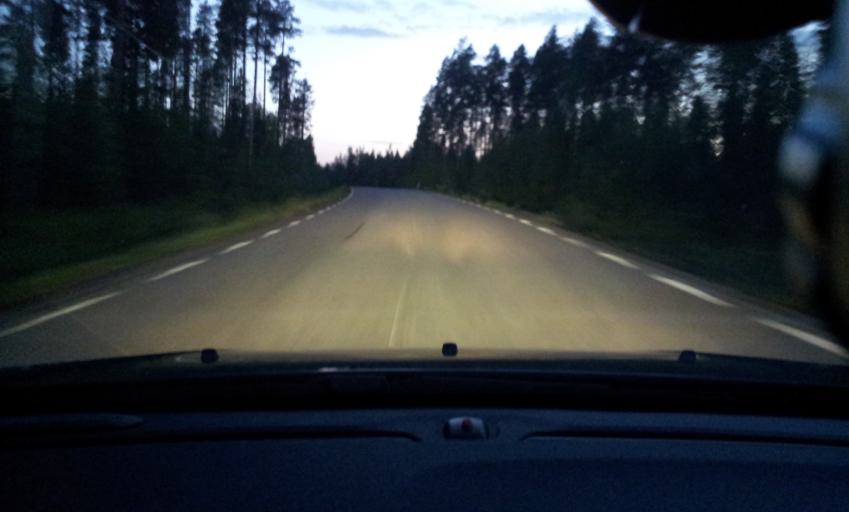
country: SE
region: Jaemtland
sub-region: Bergs Kommun
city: Hoverberg
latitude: 62.6605
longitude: 14.7784
